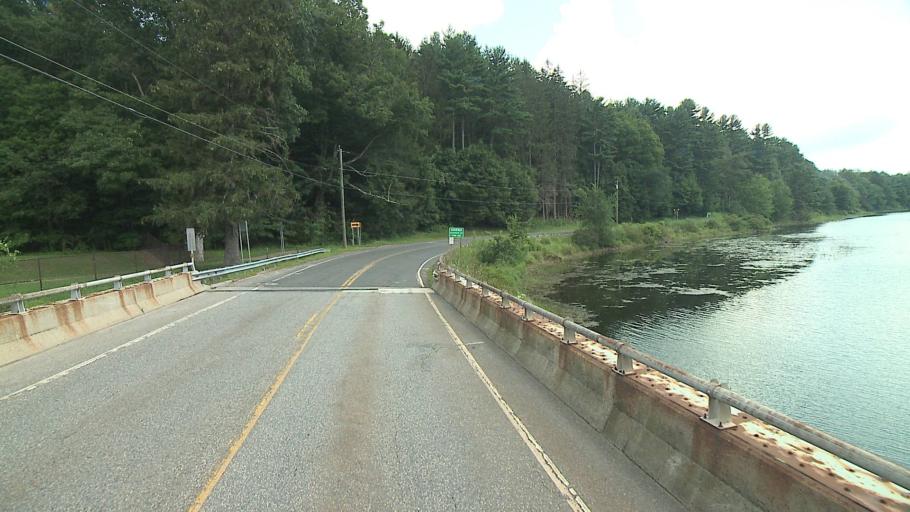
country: US
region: Connecticut
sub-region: Litchfield County
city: Bethlehem Village
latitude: 41.6732
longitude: -73.1426
